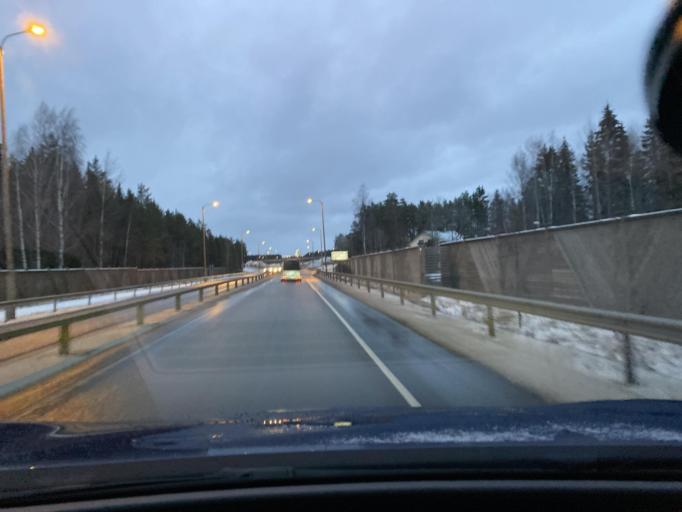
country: FI
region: Satakunta
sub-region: Rauma
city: Rauma
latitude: 61.1470
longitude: 21.5608
